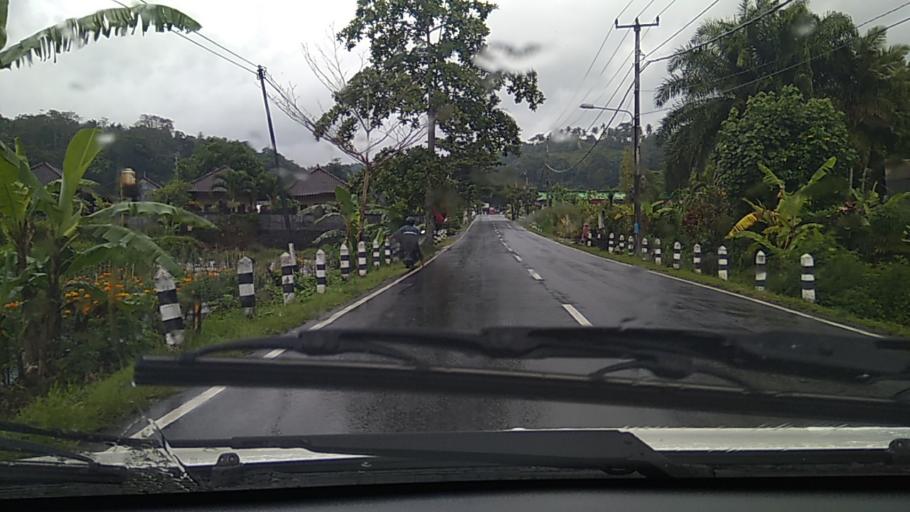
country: ID
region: Bali
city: Banjar Ababi
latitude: -8.4141
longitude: 115.5890
